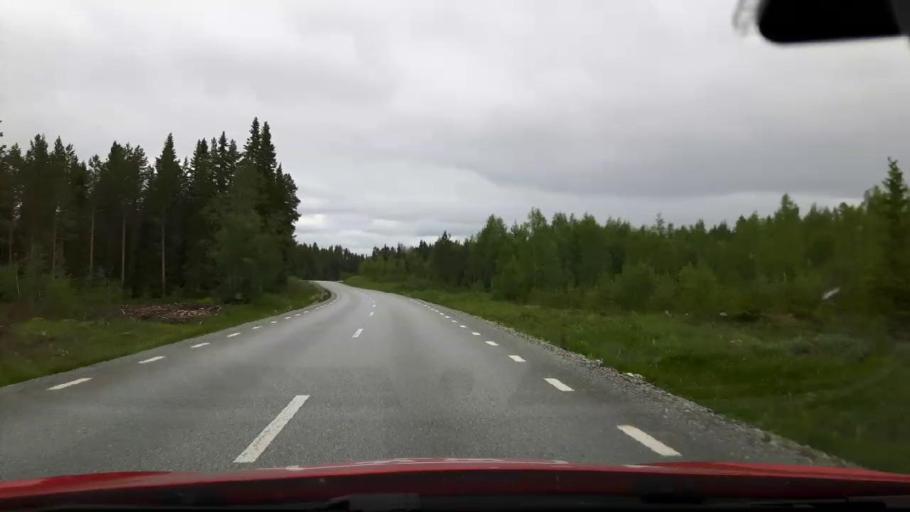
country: SE
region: Jaemtland
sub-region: OEstersunds Kommun
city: Lit
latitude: 63.7072
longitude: 14.6929
